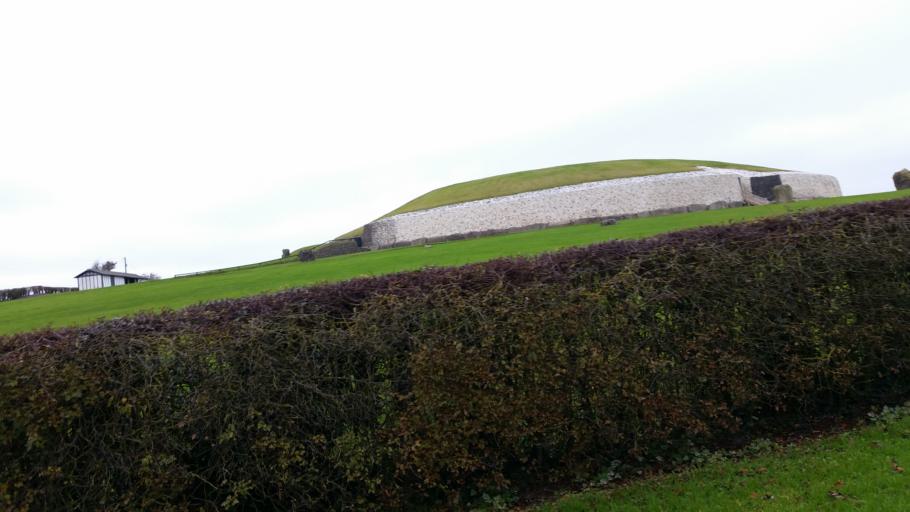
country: IE
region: Leinster
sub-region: An Mhi
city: Duleek
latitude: 53.6936
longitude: -6.4755
